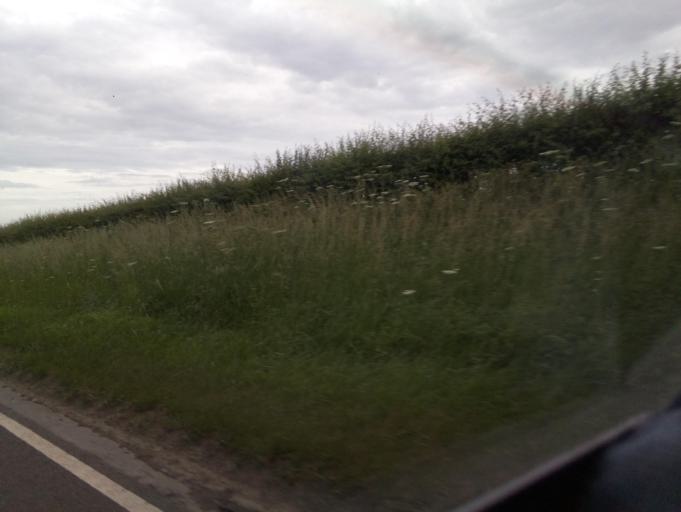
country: GB
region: England
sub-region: Dorset
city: Sherborne
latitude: 50.9462
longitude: -2.5466
